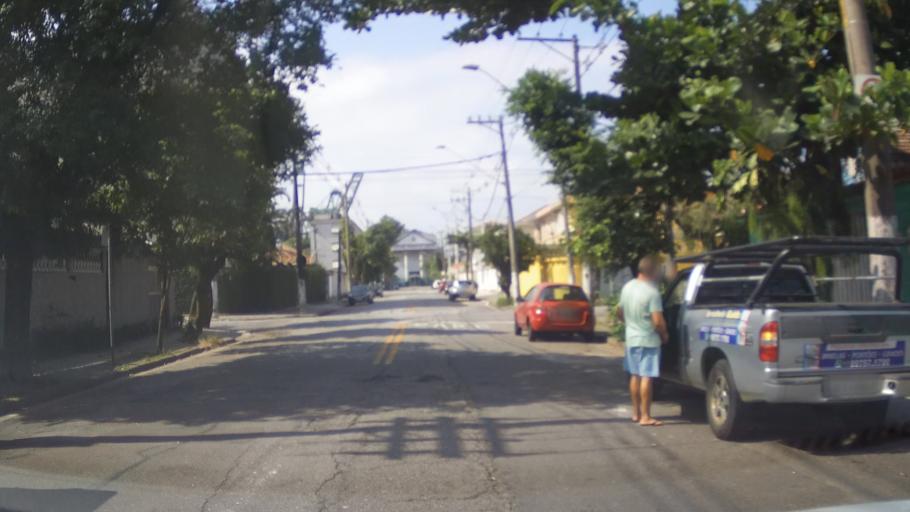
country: BR
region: Sao Paulo
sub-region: Santos
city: Santos
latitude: -23.9743
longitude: -46.3000
